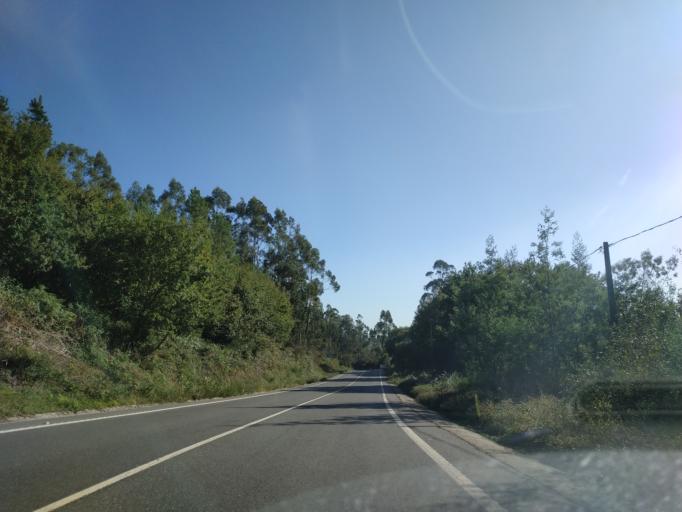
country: ES
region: Galicia
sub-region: Provincia da Coruna
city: Negreira
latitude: 42.9704
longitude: -8.7569
